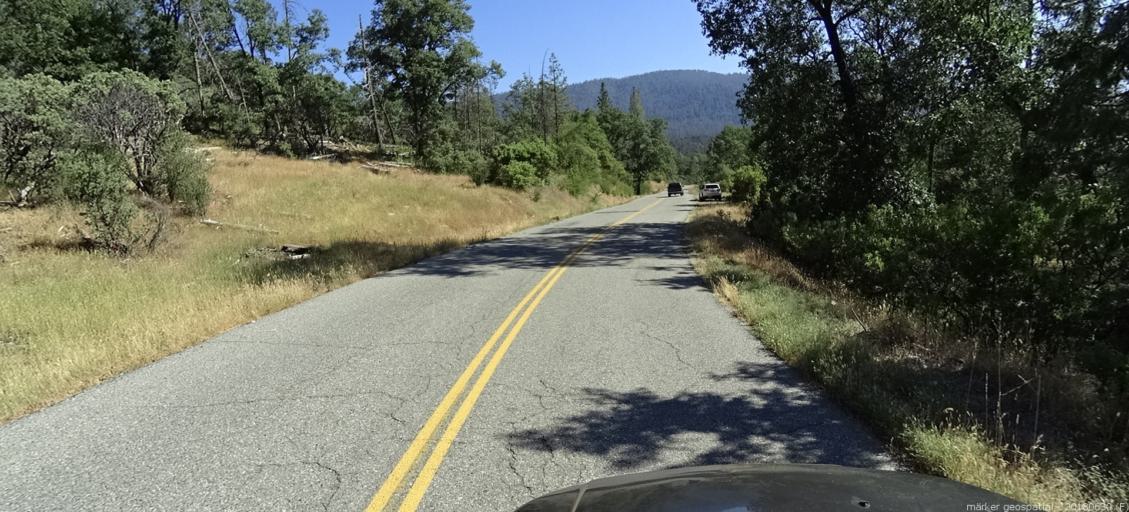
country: US
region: California
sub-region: Fresno County
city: Auberry
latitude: 37.1951
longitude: -119.4209
